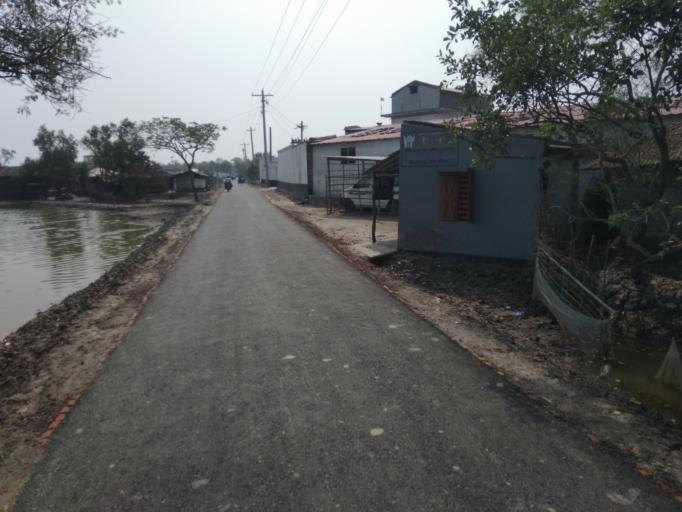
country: IN
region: West Bengal
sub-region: North 24 Parganas
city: Gosaba
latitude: 22.2624
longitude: 89.2227
